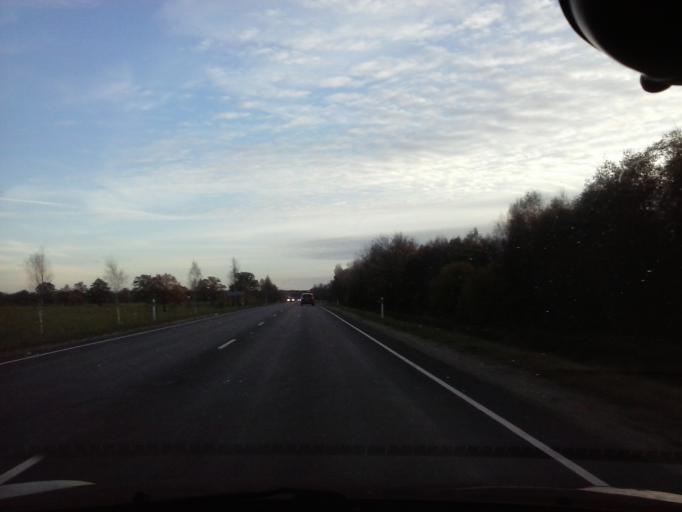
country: EE
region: Harju
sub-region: Nissi vald
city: Turba
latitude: 58.9132
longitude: 24.1116
